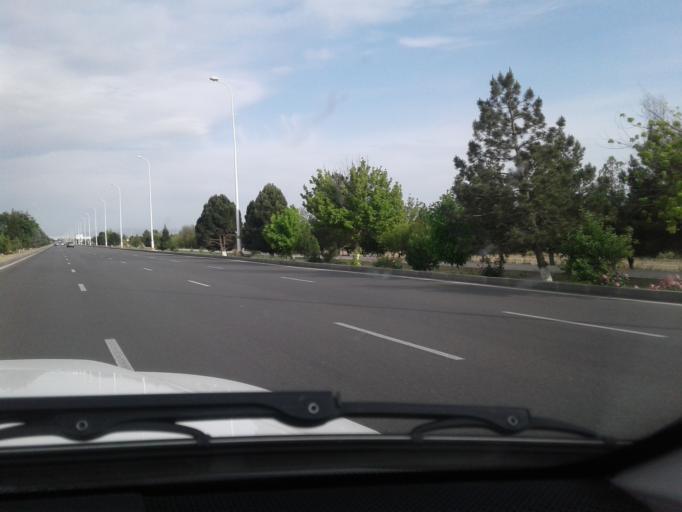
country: TM
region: Ahal
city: Ashgabat
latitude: 38.0029
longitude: 58.2944
